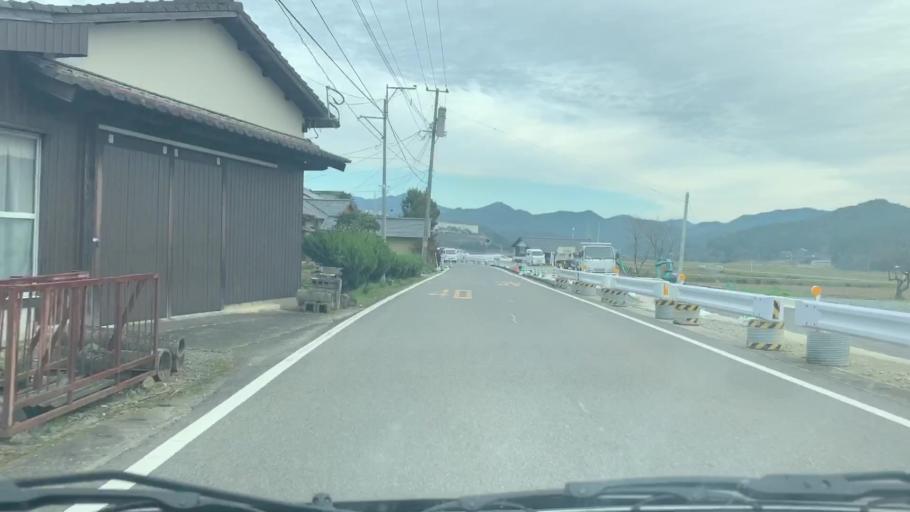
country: JP
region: Saga Prefecture
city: Takeocho-takeo
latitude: 33.2019
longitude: 129.9614
